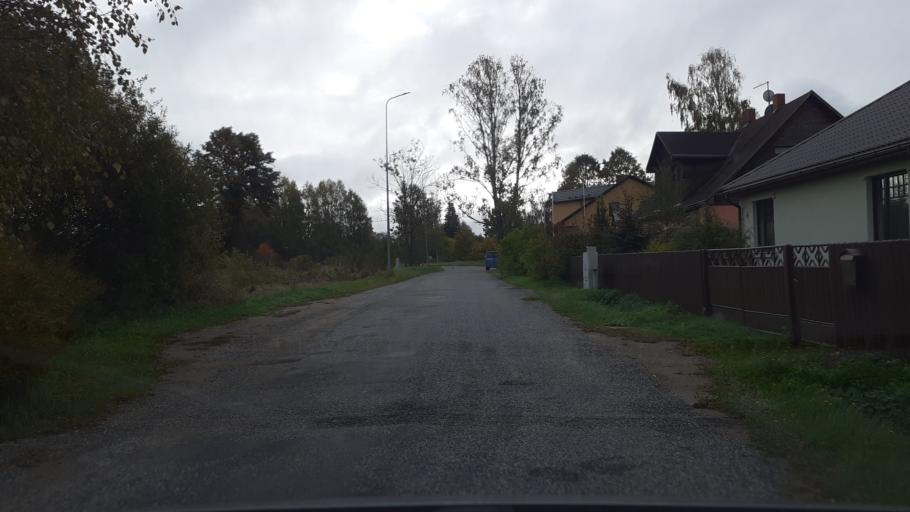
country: LV
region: Kuldigas Rajons
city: Kuldiga
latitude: 56.9596
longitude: 21.9700
